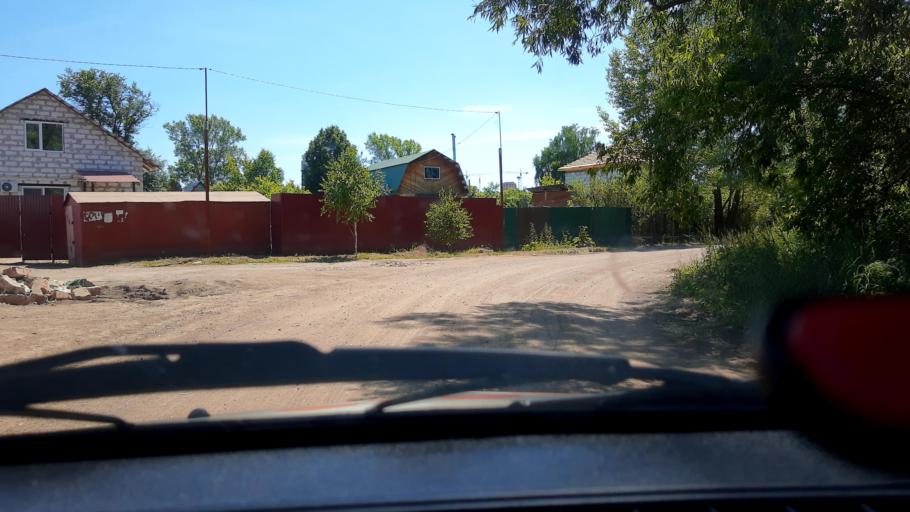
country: RU
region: Bashkortostan
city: Mikhaylovka
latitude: 54.7073
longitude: 55.8654
